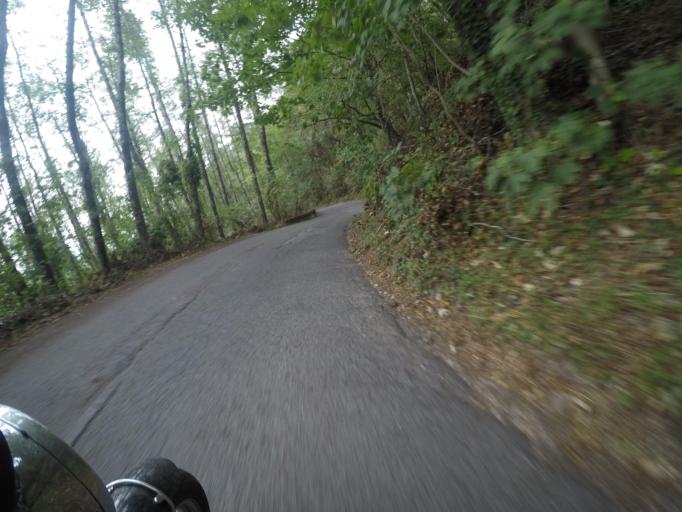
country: IT
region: Tuscany
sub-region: Provincia di Massa-Carrara
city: Carrara
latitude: 44.1205
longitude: 10.1003
